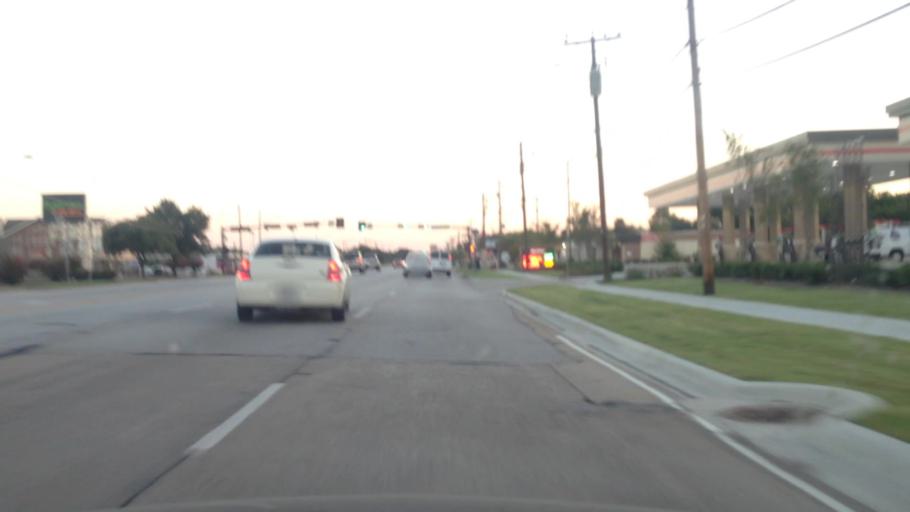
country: US
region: Texas
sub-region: Tarrant County
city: North Richland Hills
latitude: 32.8377
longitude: -97.2142
